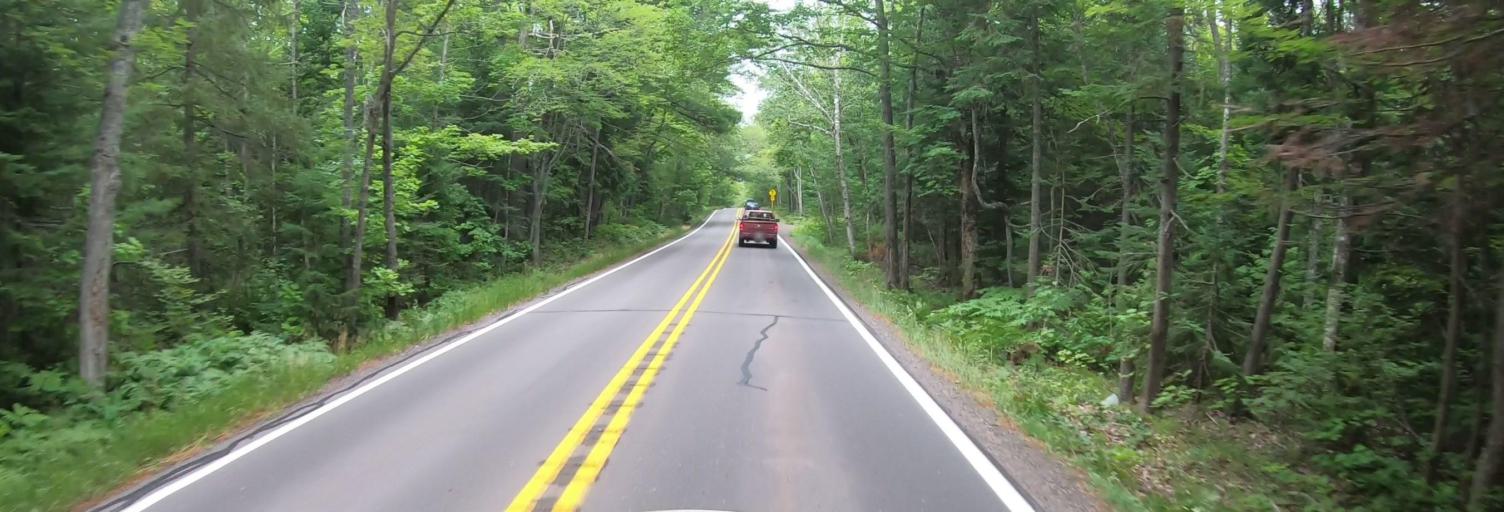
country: US
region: Michigan
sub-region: Keweenaw County
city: Eagle River
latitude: 47.4446
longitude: -87.9316
